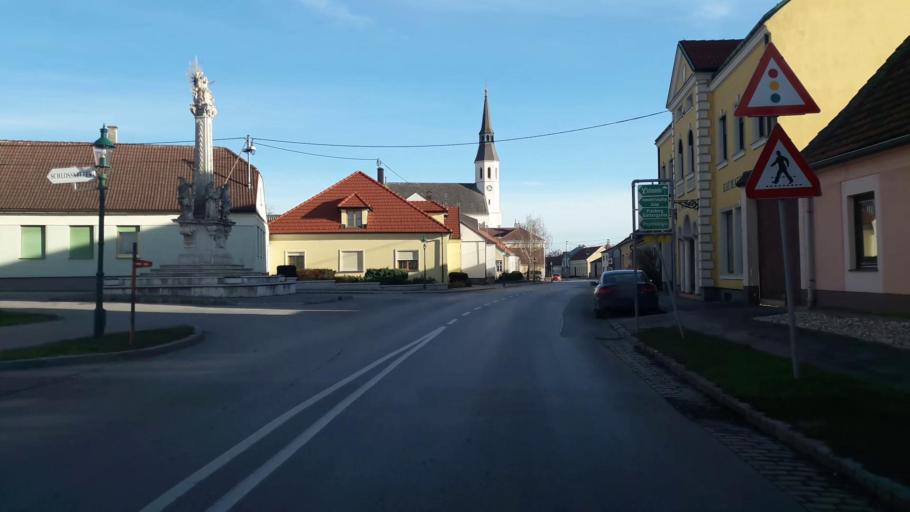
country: AT
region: Lower Austria
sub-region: Politischer Bezirk Mistelbach
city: Bockfliess
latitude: 48.3602
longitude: 16.6016
